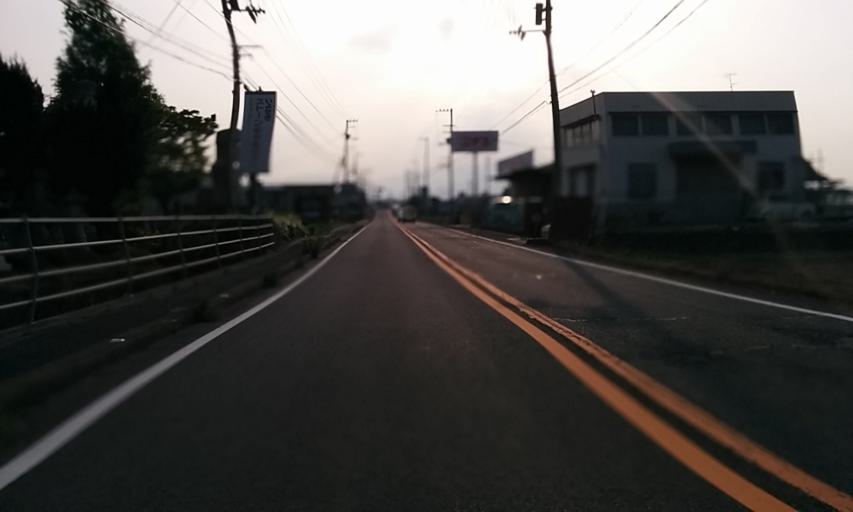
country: JP
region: Ehime
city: Saijo
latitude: 33.8950
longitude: 133.1616
